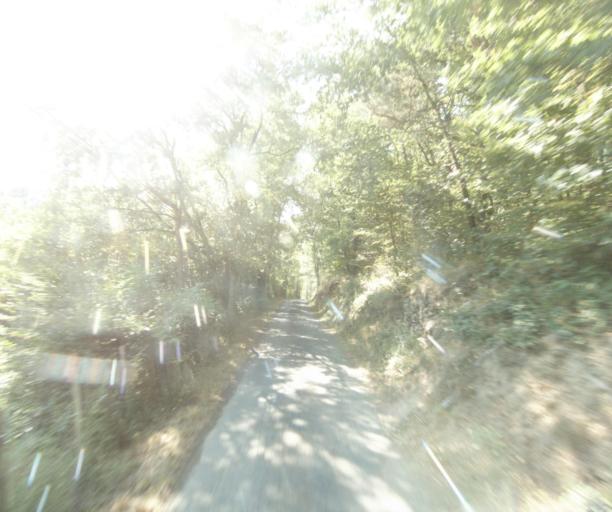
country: FR
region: Rhone-Alpes
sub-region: Departement du Rhone
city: Courzieu
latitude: 45.7678
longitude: 4.5849
